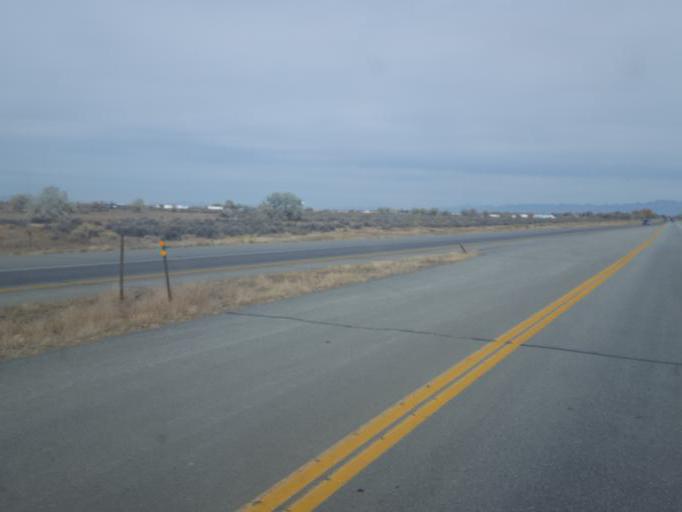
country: US
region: Colorado
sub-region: Alamosa County
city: Alamosa
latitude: 37.4327
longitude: -105.8893
